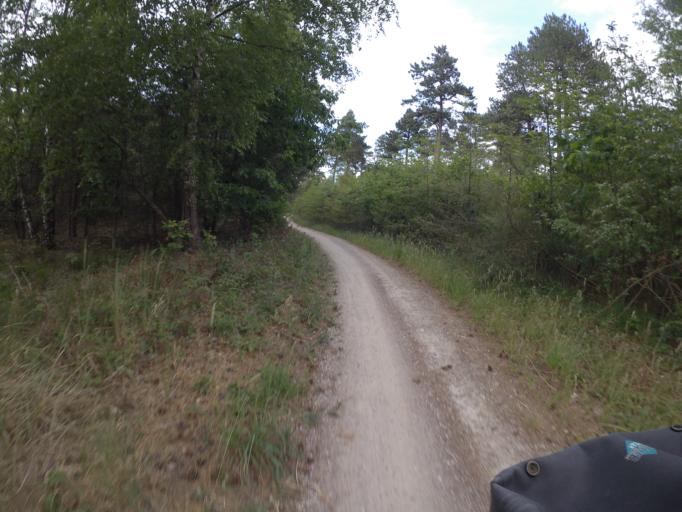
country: NL
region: North Brabant
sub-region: Gemeente Oirschot
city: Oostelbeers
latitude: 51.4390
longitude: 5.2934
